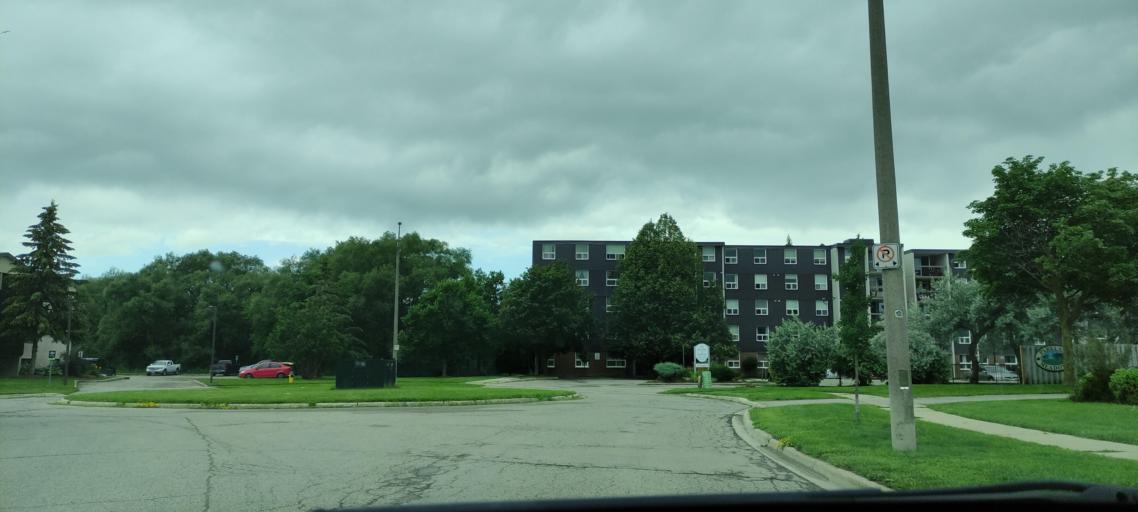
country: CA
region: Ontario
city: Stratford
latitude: 43.3850
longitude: -80.9763
